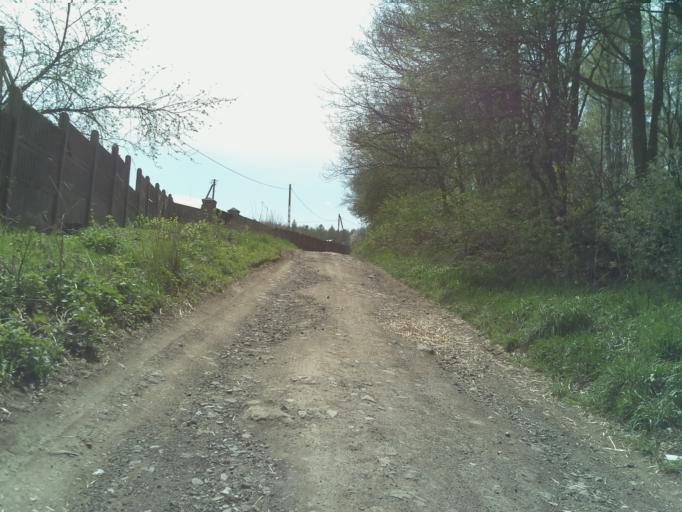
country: PL
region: Lower Silesian Voivodeship
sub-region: Powiat swidnicki
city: Swiebodzice
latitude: 50.8257
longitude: 16.3240
